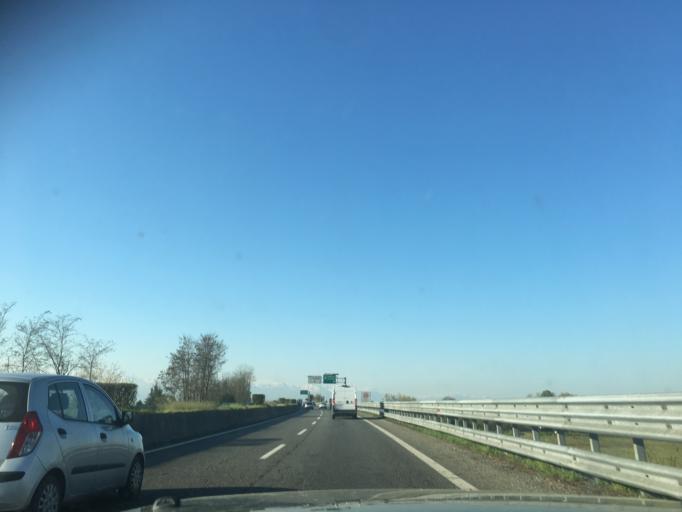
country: IT
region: Piedmont
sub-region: Provincia di Torino
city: Borgaro Torinese
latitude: 45.1224
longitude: 7.6958
